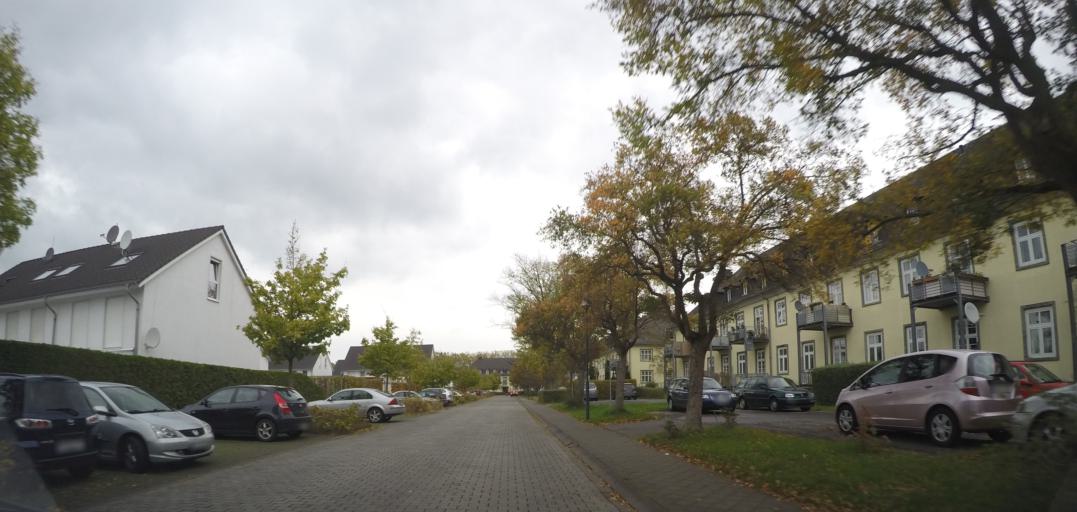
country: DE
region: North Rhine-Westphalia
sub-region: Regierungsbezirk Arnsberg
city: Lippstadt
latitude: 51.6595
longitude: 8.3483
